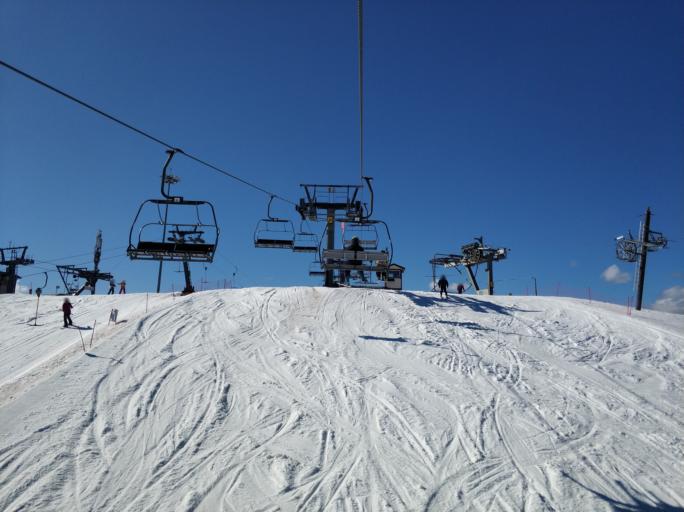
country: RU
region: Leningrad
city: Sosnovo
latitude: 60.5148
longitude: 30.2141
